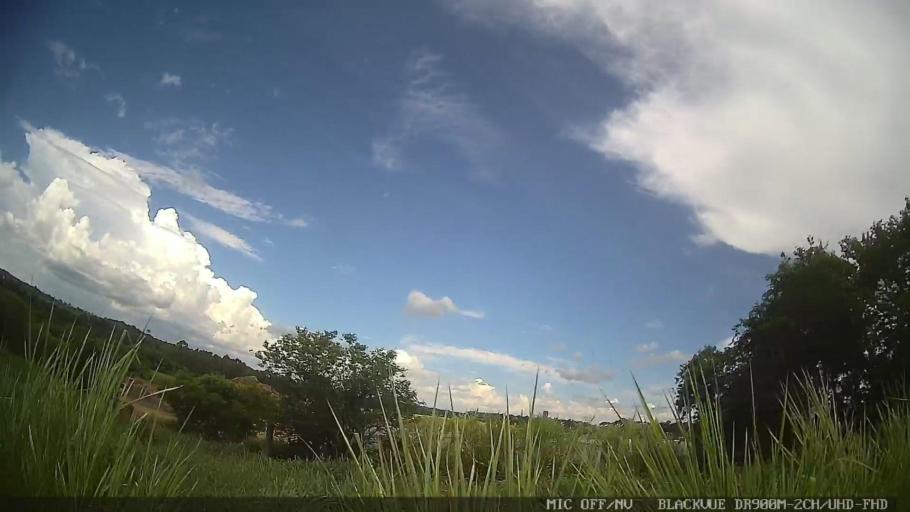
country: BR
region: Sao Paulo
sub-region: Conchas
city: Conchas
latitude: -23.0211
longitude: -47.9979
